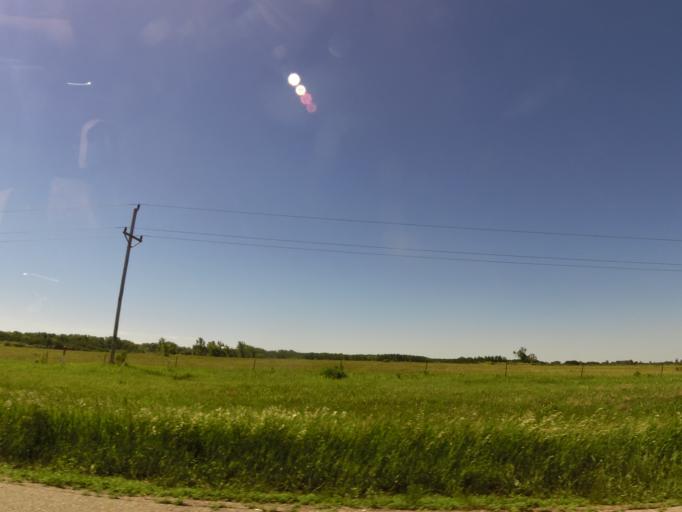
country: US
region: Minnesota
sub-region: Polk County
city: Crookston
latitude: 47.7604
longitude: -96.4203
